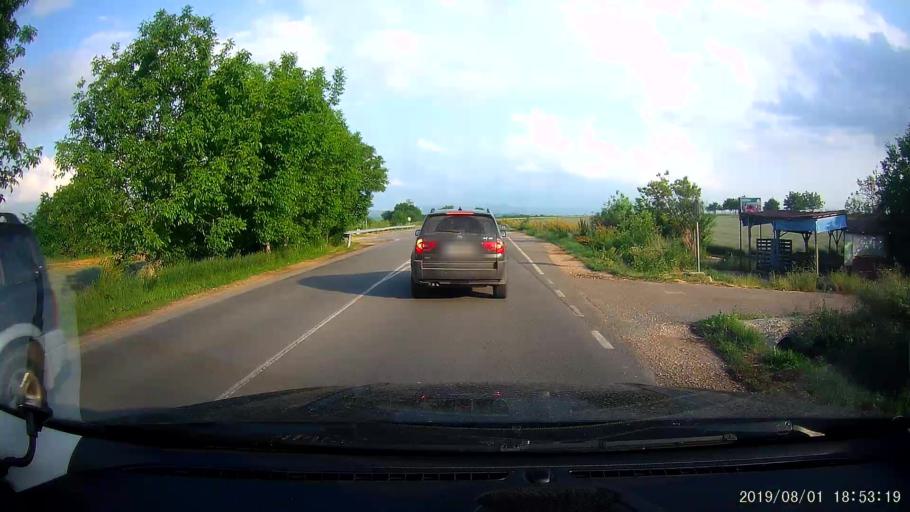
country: BG
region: Shumen
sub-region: Obshtina Shumen
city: Shumen
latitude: 43.2227
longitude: 26.9923
